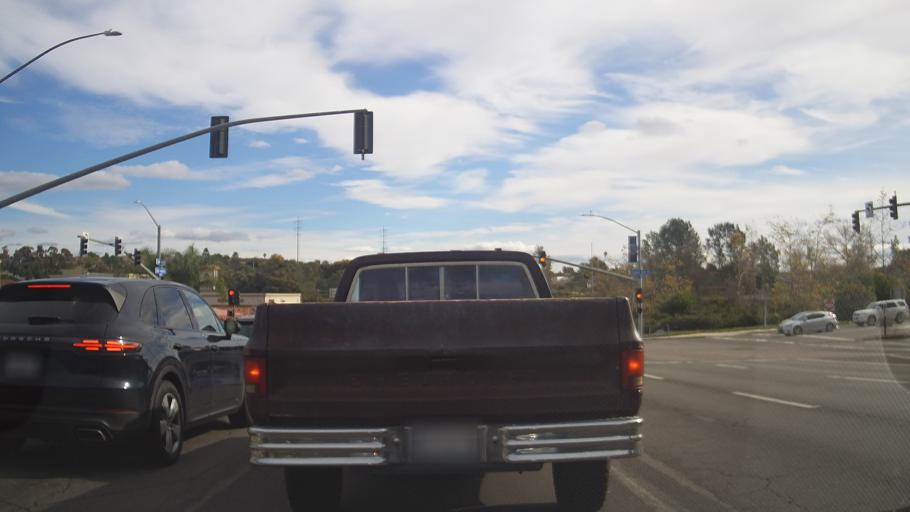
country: US
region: California
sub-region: San Diego County
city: Fairbanks Ranch
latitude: 32.9596
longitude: -117.1161
